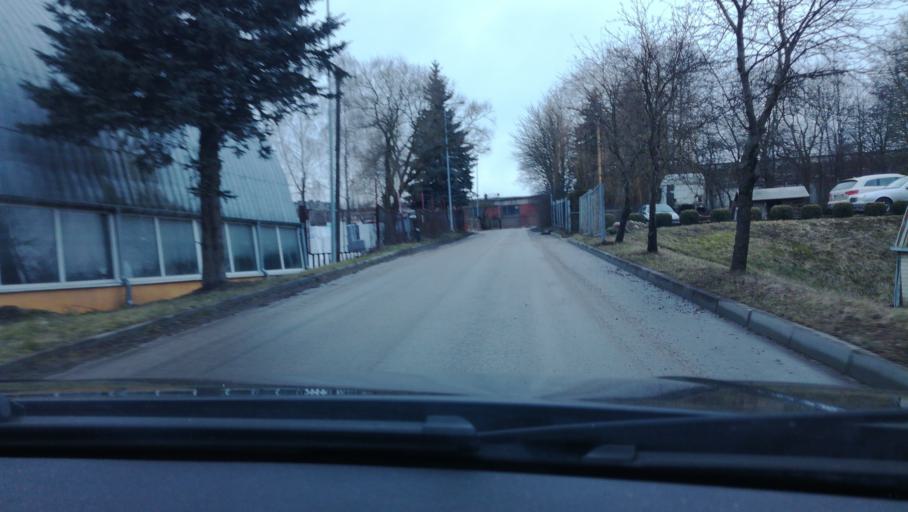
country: LT
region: Alytaus apskritis
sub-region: Alytus
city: Alytus
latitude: 54.3902
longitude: 24.0348
